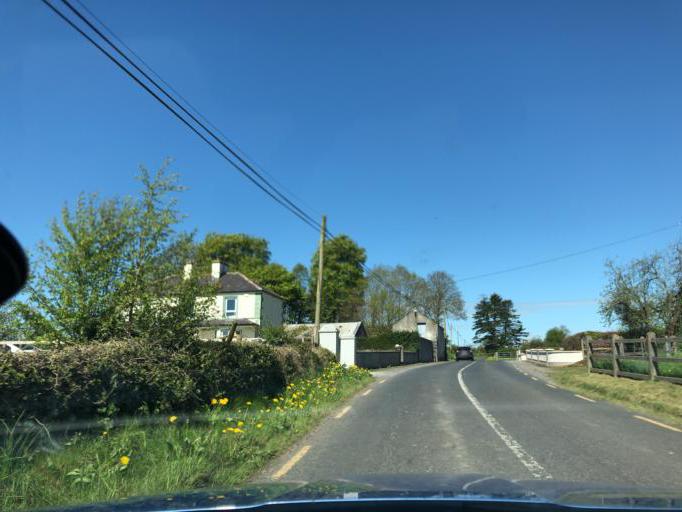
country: IE
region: Connaught
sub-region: County Galway
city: Portumna
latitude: 53.1357
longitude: -8.3609
